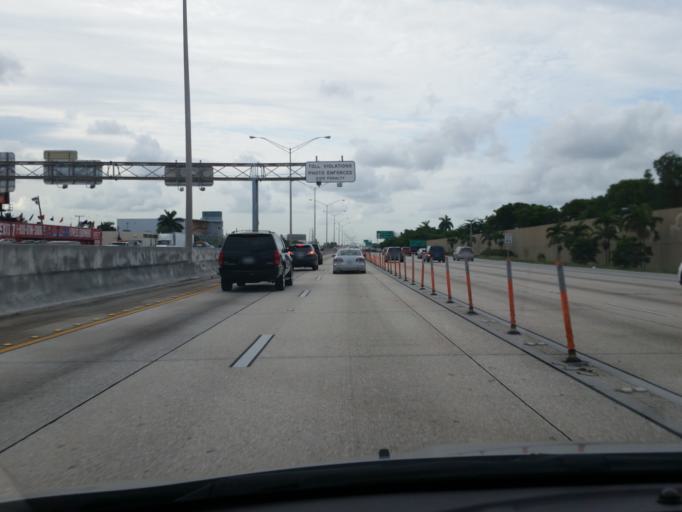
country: US
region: Florida
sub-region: Miami-Dade County
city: El Portal
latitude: 25.8515
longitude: -80.2079
